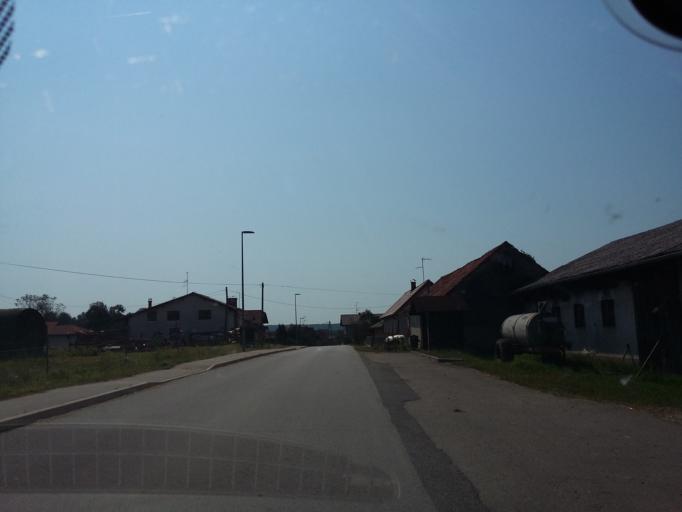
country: SI
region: Hodos-Hodos
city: Hodos
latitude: 46.8336
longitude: 16.3182
